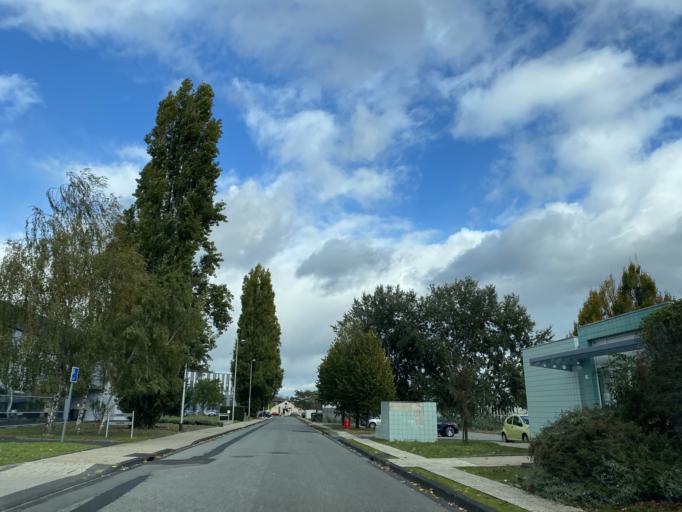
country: FR
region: Auvergne
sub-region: Departement du Puy-de-Dome
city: Aubiere
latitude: 45.7650
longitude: 3.1323
